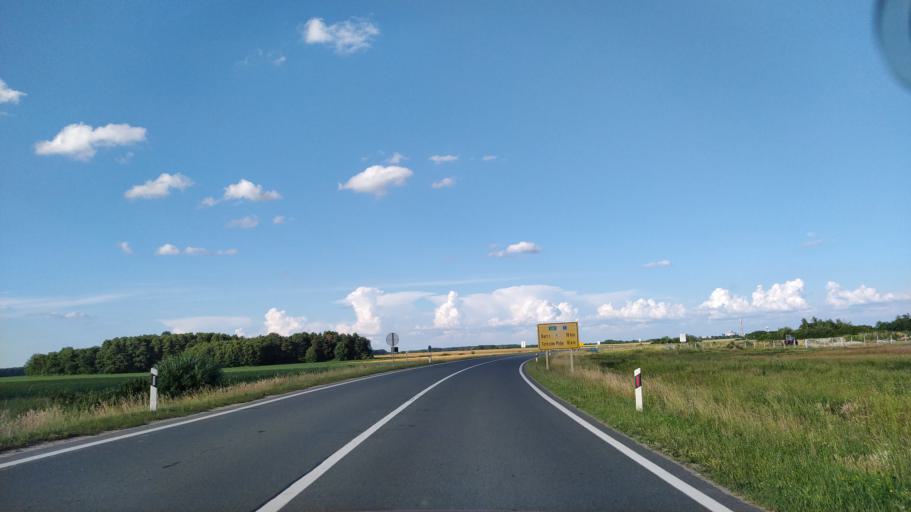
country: HR
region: Virovitick-Podravska
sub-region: Grad Virovitica
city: Virovitica
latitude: 45.8468
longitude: 17.3553
